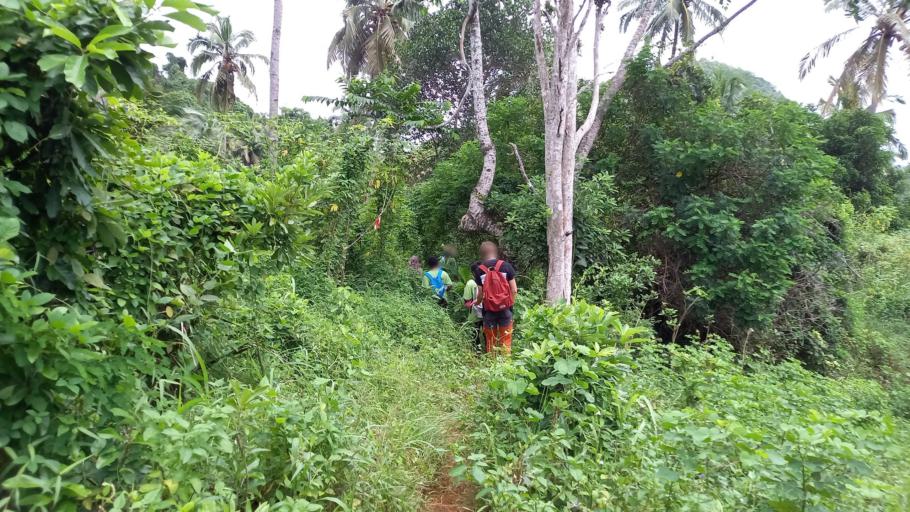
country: YT
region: Acoua
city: Acoua
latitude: -12.7112
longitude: 45.0582
